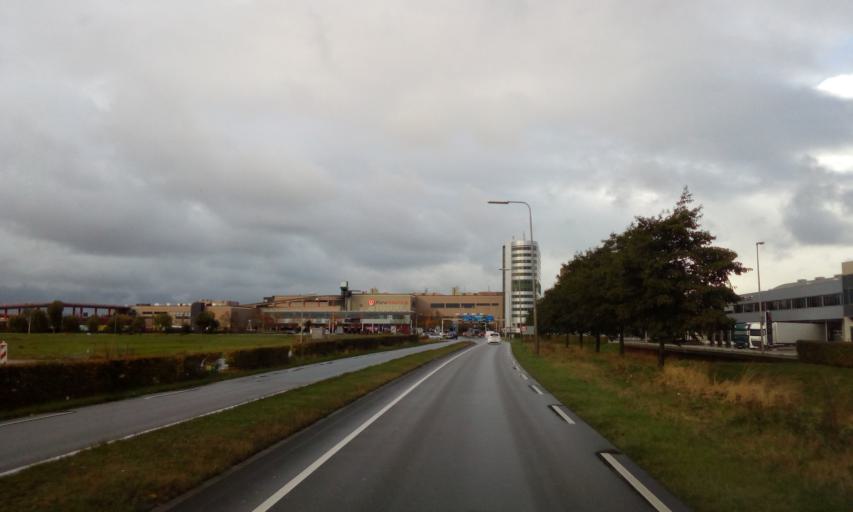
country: NL
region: South Holland
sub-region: Gemeente Westland
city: Honselersdijk
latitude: 51.9944
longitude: 4.2319
